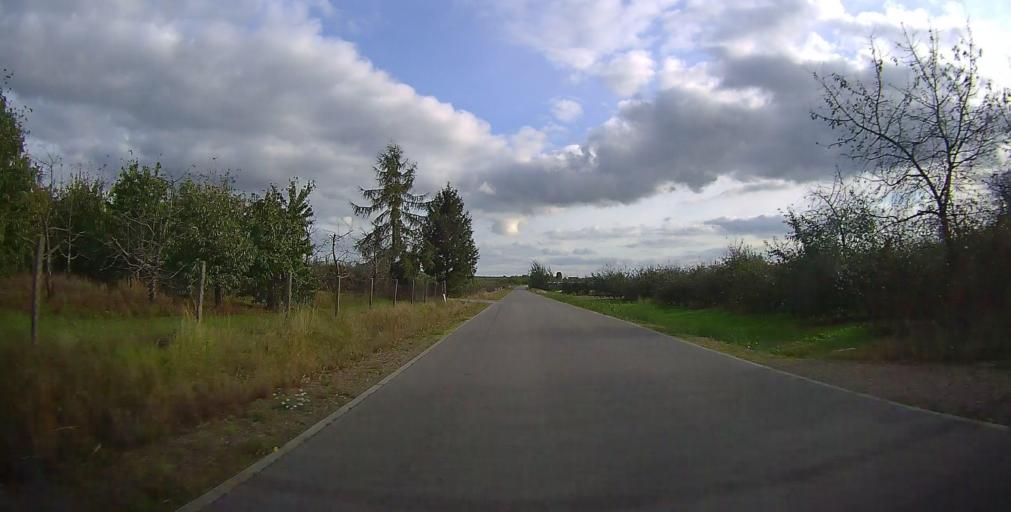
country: PL
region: Masovian Voivodeship
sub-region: Powiat bialobrzeski
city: Promna
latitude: 51.7483
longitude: 20.9635
